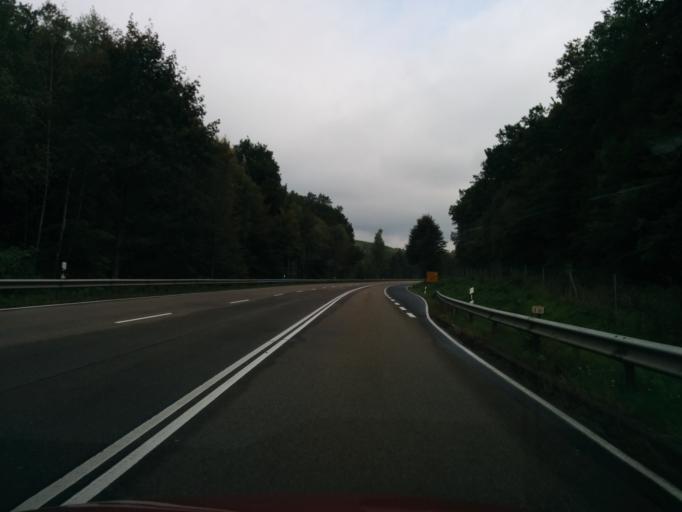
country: DE
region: Rheinland-Pfalz
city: Eitelborn
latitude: 50.3670
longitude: 7.6905
